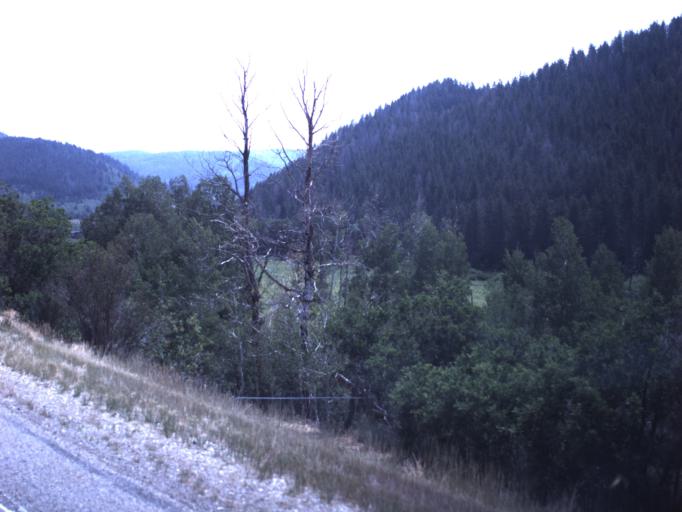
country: US
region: Utah
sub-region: Summit County
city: Francis
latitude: 40.5591
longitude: -111.1259
